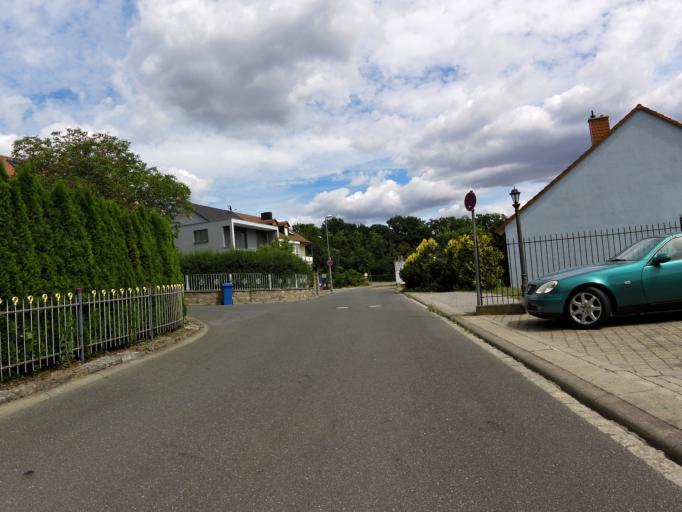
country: DE
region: Bavaria
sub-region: Regierungsbezirk Unterfranken
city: Veitshochheim
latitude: 49.8126
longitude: 9.8934
